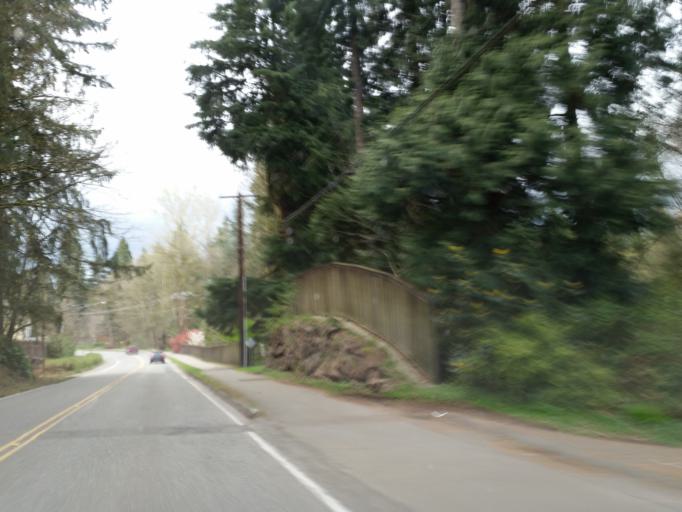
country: US
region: Washington
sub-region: King County
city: Woodinville
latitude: 47.7639
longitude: -122.1636
